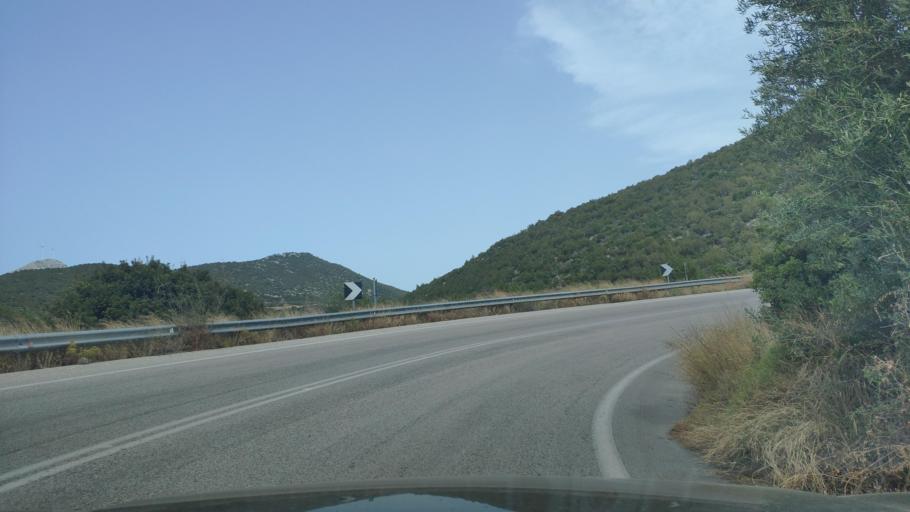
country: GR
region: Peloponnese
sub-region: Nomos Argolidos
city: Didyma
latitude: 37.5111
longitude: 23.1997
